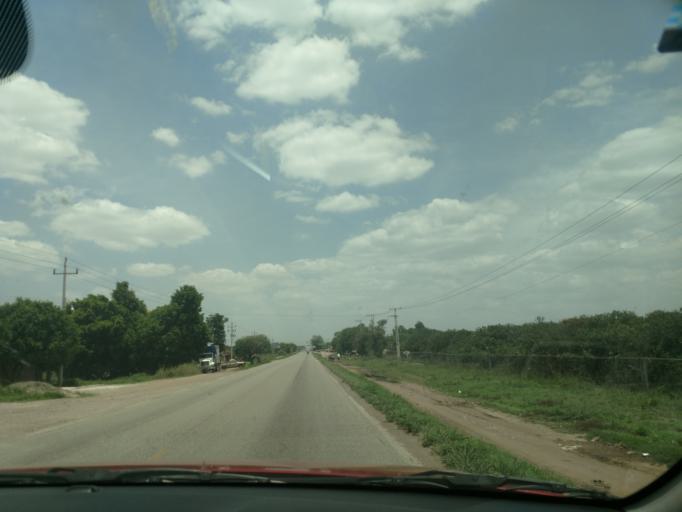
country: MX
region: San Luis Potosi
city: Ciudad Fernandez
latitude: 21.9490
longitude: -100.0594
